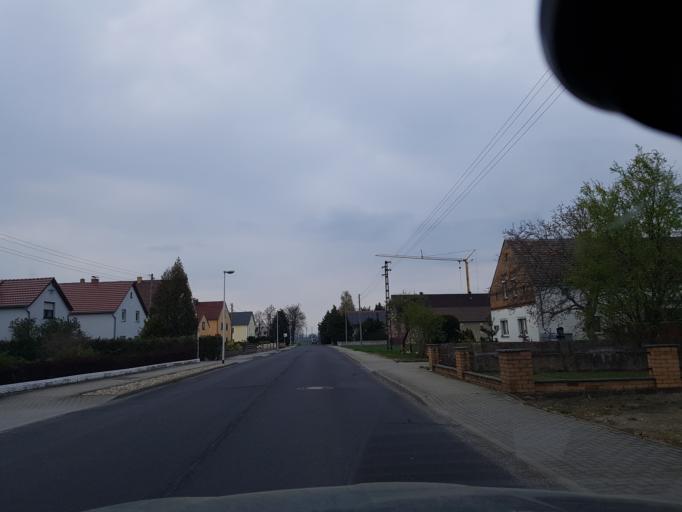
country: DE
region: Brandenburg
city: Grosskmehlen
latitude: 51.3876
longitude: 13.7108
